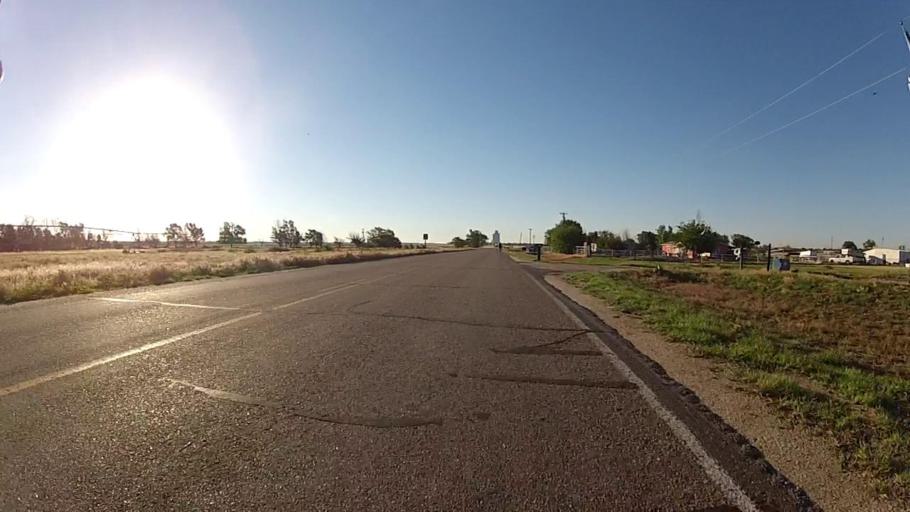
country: US
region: Kansas
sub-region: Ford County
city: Dodge City
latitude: 37.7074
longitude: -99.9088
